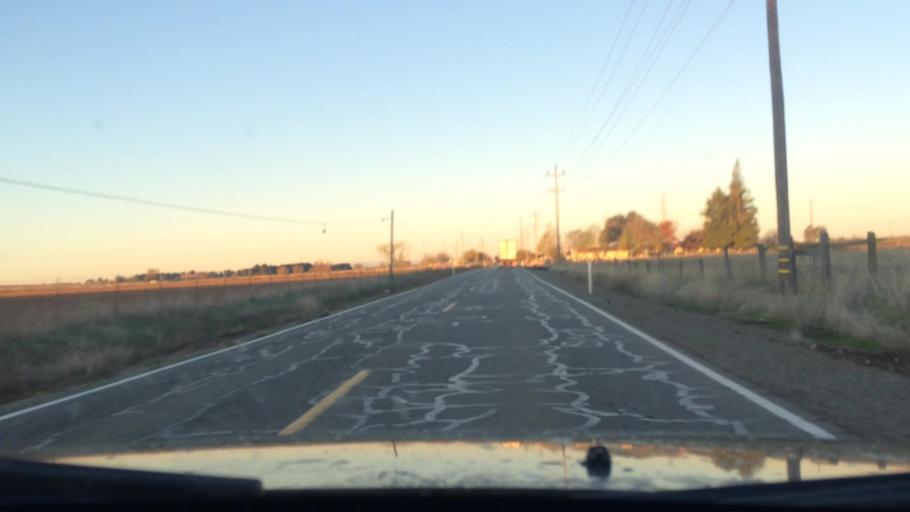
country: US
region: California
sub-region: Sacramento County
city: Vineyard
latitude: 38.5109
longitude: -121.3099
